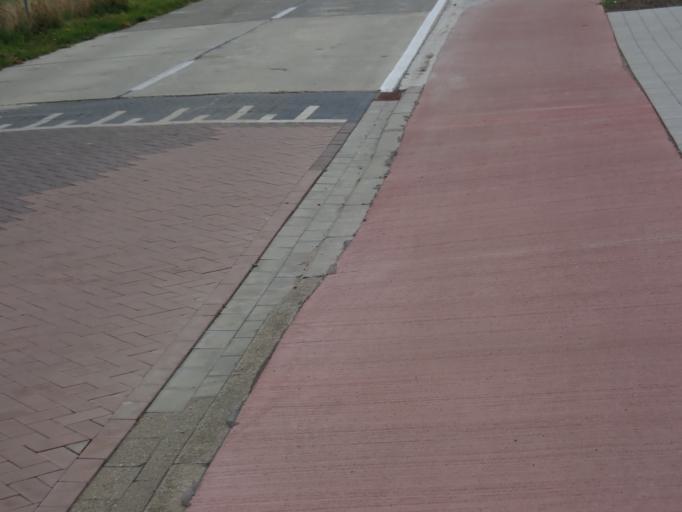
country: BE
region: Flanders
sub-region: Provincie Antwerpen
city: Berlaar
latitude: 51.1371
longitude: 4.6342
